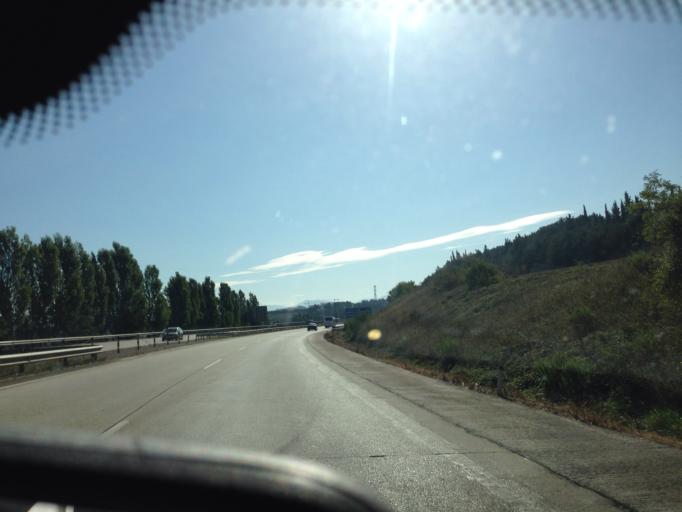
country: ES
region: Navarre
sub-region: Provincia de Navarra
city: Baranain
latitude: 42.7912
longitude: -1.6703
